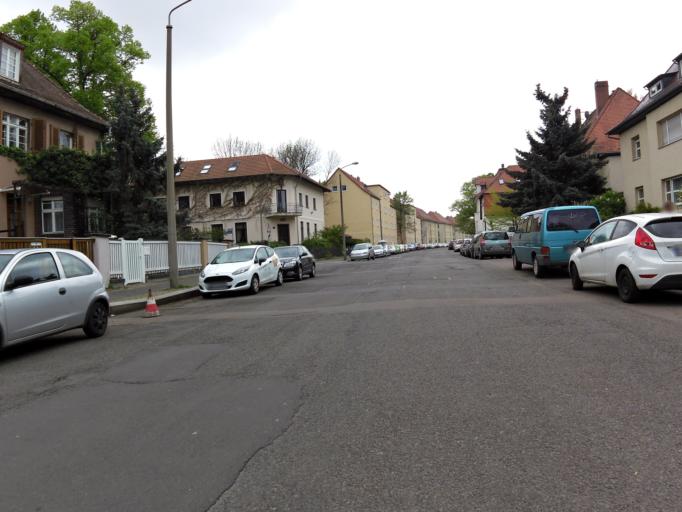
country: DE
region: Saxony
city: Leipzig
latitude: 51.3656
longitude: 12.3819
